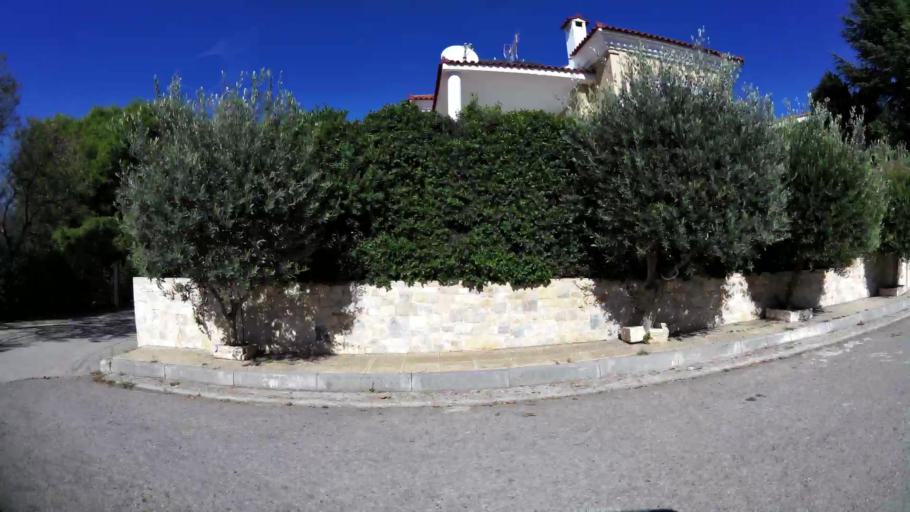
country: GR
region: Attica
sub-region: Nomarchia Athinas
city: Nea Erythraia
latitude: 38.1019
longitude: 23.8190
